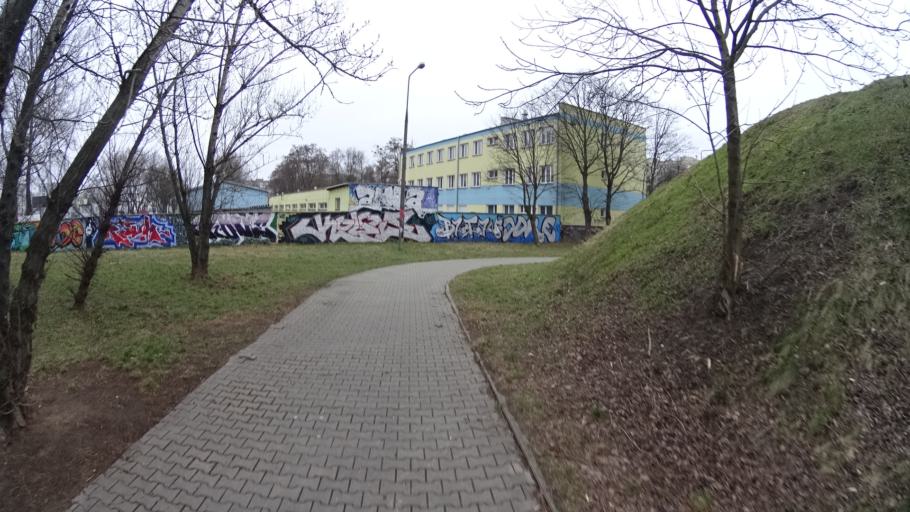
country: PL
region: Masovian Voivodeship
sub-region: Warszawa
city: Bemowo
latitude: 52.2386
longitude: 20.9010
